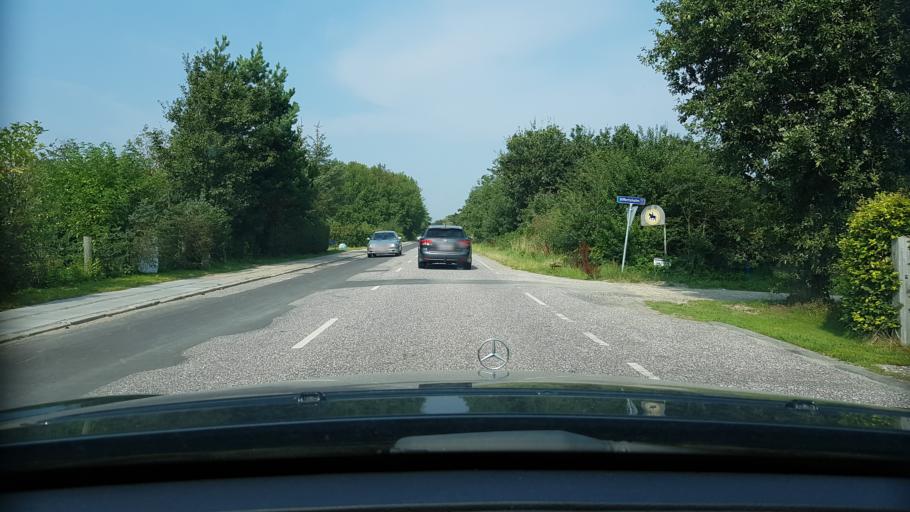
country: DK
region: North Denmark
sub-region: Mariagerfjord Kommune
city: Hadsund
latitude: 56.8133
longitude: 10.2710
